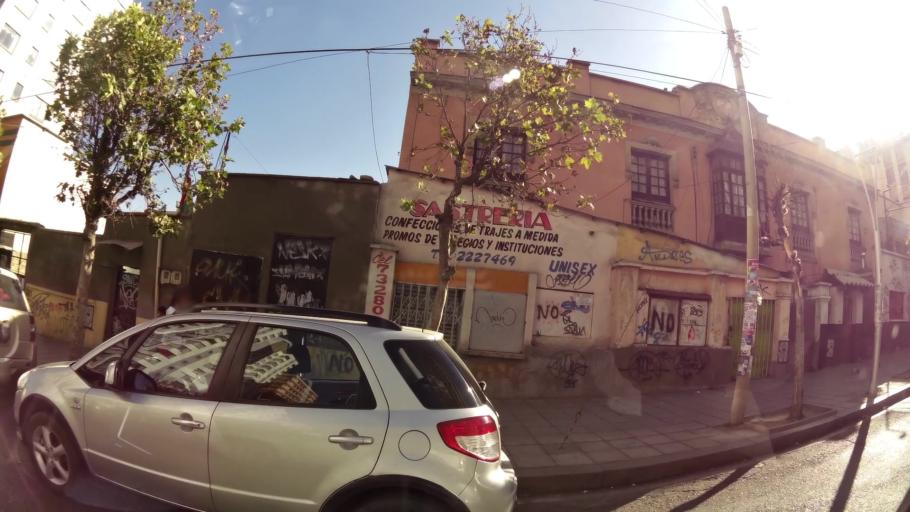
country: BO
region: La Paz
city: La Paz
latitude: -16.5033
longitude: -68.1218
